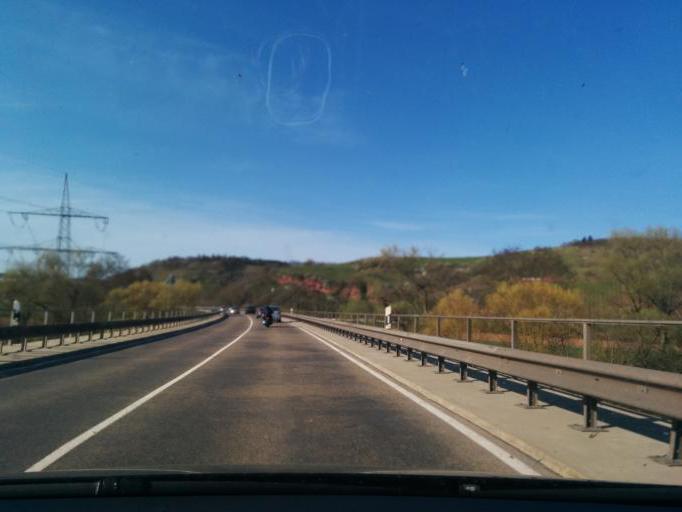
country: DE
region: Rheinland-Pfalz
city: Windesheim
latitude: 49.9031
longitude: 7.8245
